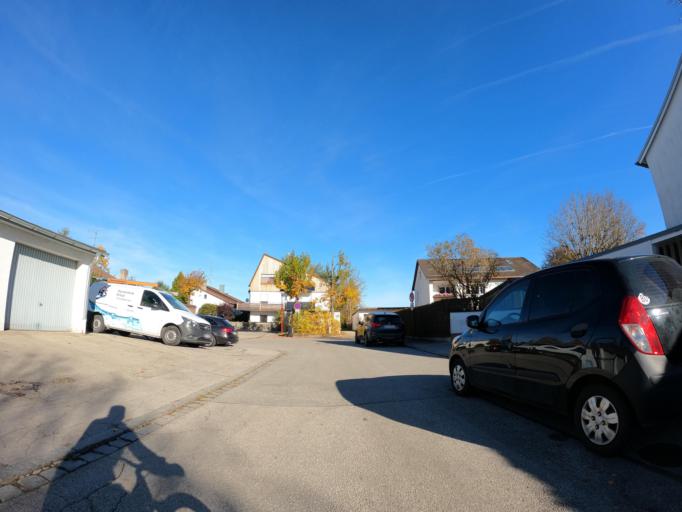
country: DE
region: Bavaria
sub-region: Upper Bavaria
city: Oberhaching
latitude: 48.0243
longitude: 11.6025
